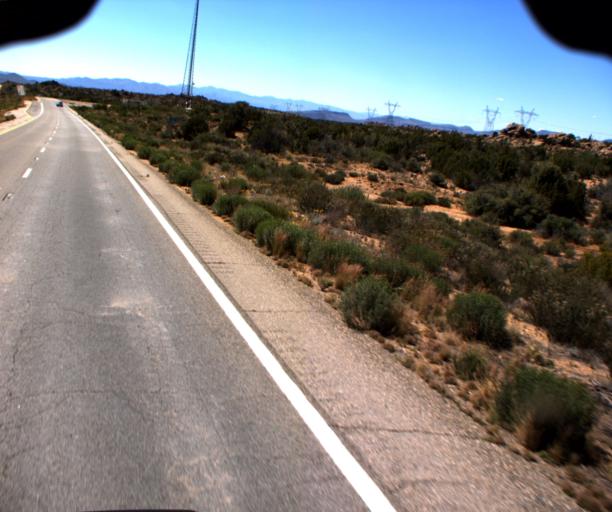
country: US
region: Arizona
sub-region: Yavapai County
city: Bagdad
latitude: 34.4784
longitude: -113.3328
